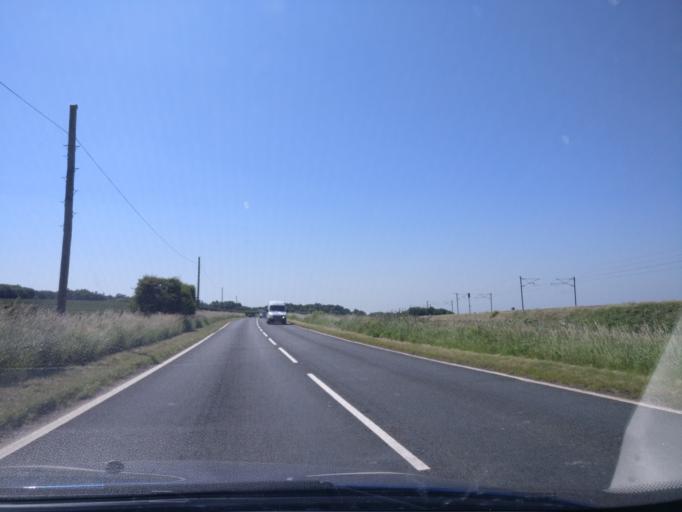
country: GB
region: Scotland
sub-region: East Lothian
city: Gullane
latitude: 55.9891
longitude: -2.8381
